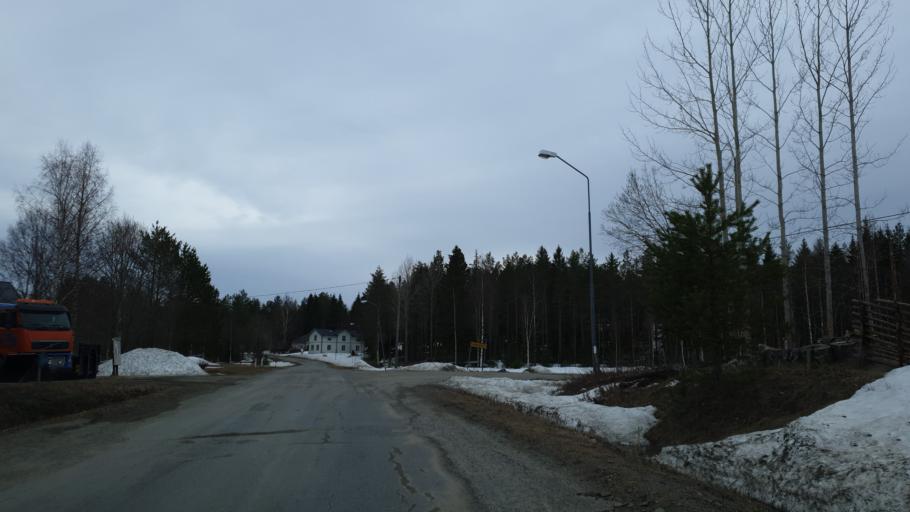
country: SE
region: Vaesterbotten
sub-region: Robertsfors Kommun
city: Robertsfors
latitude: 64.3955
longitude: 21.0017
